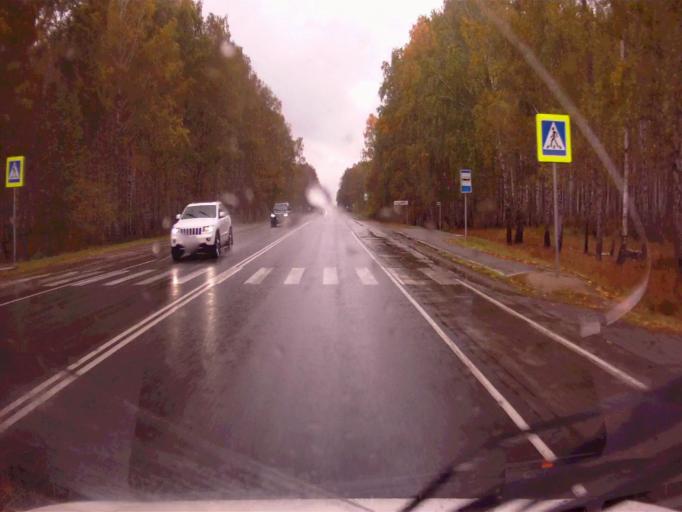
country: RU
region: Chelyabinsk
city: Argayash
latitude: 55.4121
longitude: 61.0392
